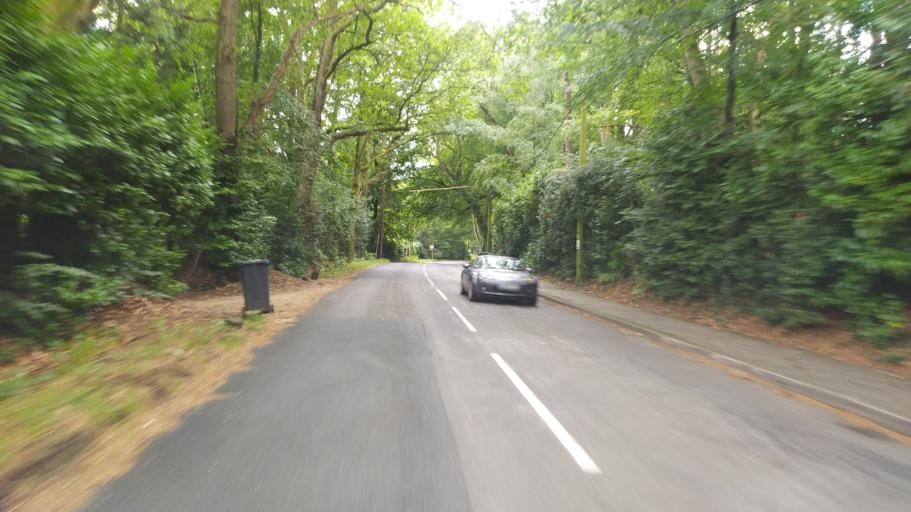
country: GB
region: England
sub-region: Hampshire
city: Romsey
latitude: 51.0110
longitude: -1.5467
